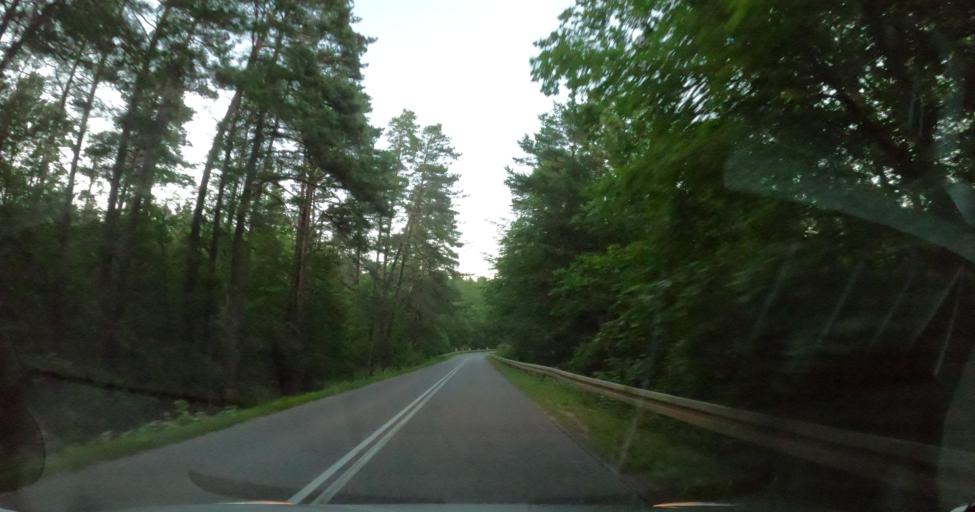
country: PL
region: Pomeranian Voivodeship
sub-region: Powiat wejherowski
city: Linia
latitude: 54.4597
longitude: 17.9553
